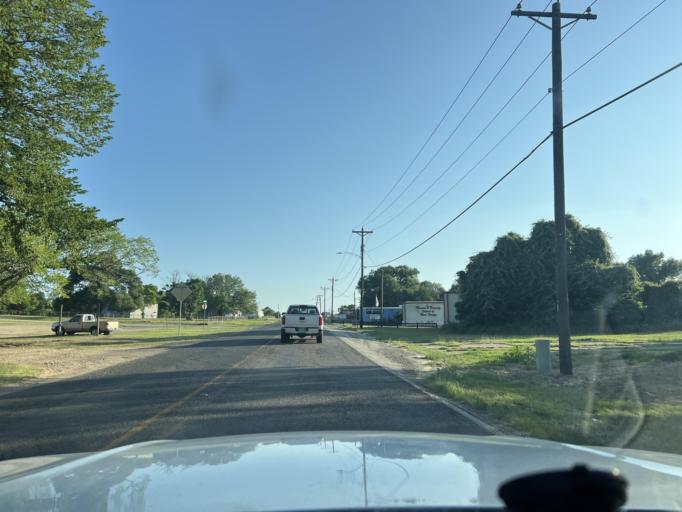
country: US
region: Texas
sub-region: Washington County
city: Brenham
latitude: 30.1766
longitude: -96.3866
